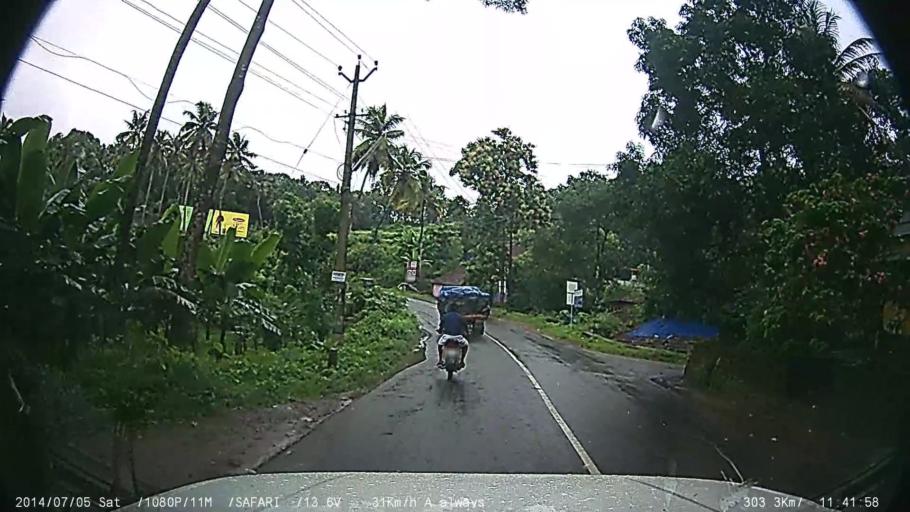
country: IN
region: Kerala
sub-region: Ernakulam
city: Muvattupuzha
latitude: 9.9675
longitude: 76.5782
